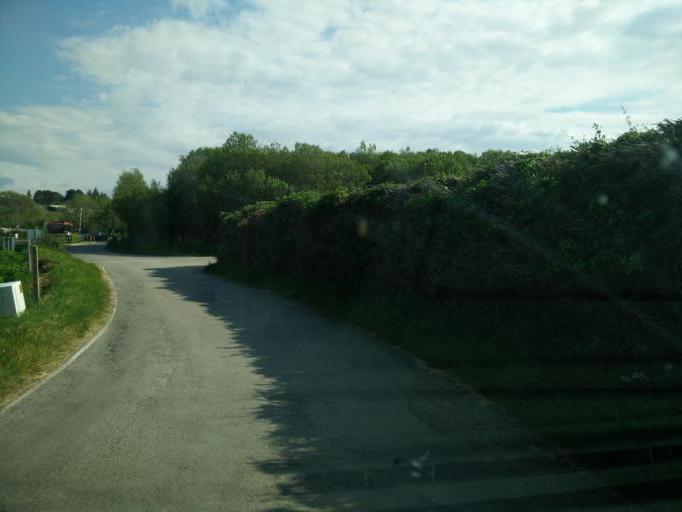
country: FR
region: Brittany
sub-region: Departement du Finistere
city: Crozon
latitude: 48.2395
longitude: -4.5452
